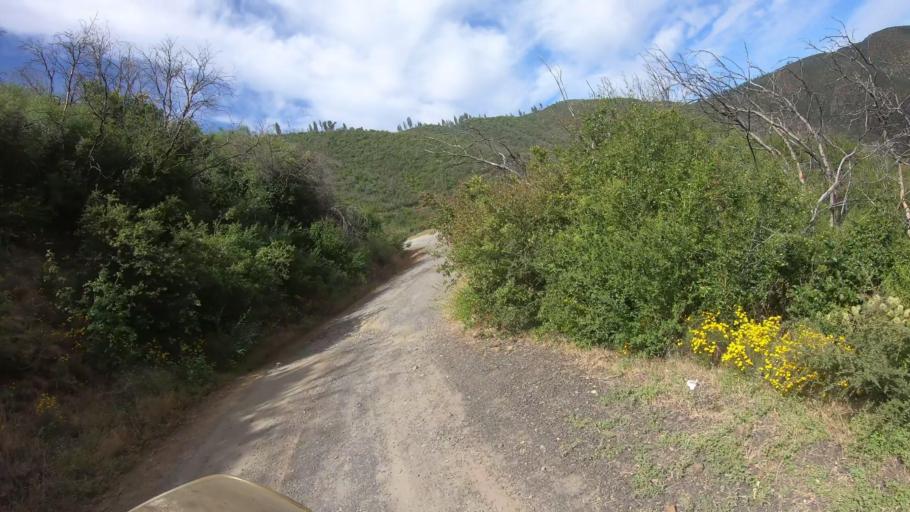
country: US
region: California
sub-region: Tuolumne County
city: Tuolumne City
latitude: 37.8344
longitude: -120.0949
